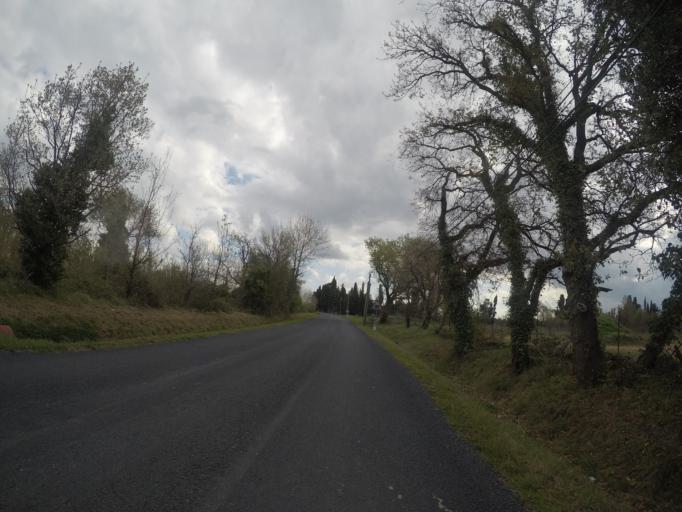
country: FR
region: Languedoc-Roussillon
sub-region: Departement des Pyrenees-Orientales
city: Le Soler
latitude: 42.6774
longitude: 2.7837
